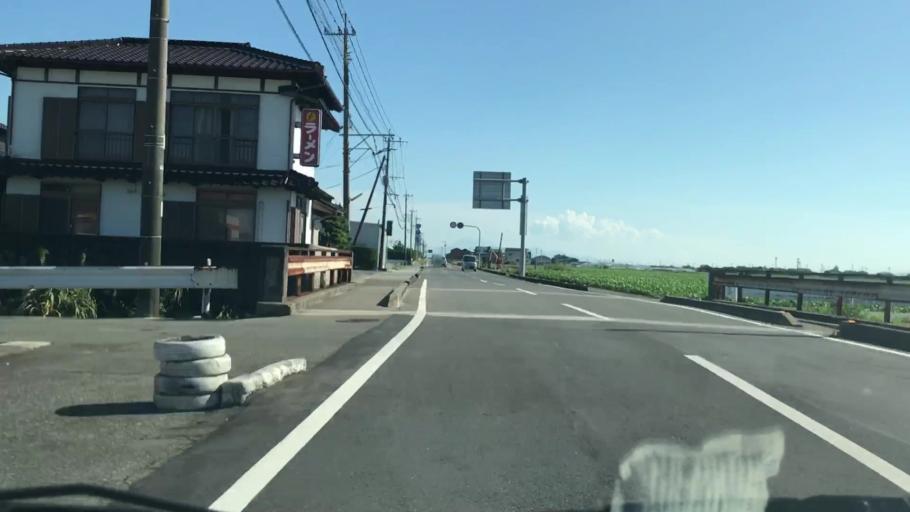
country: JP
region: Saga Prefecture
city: Okawa
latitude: 33.2035
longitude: 130.3352
